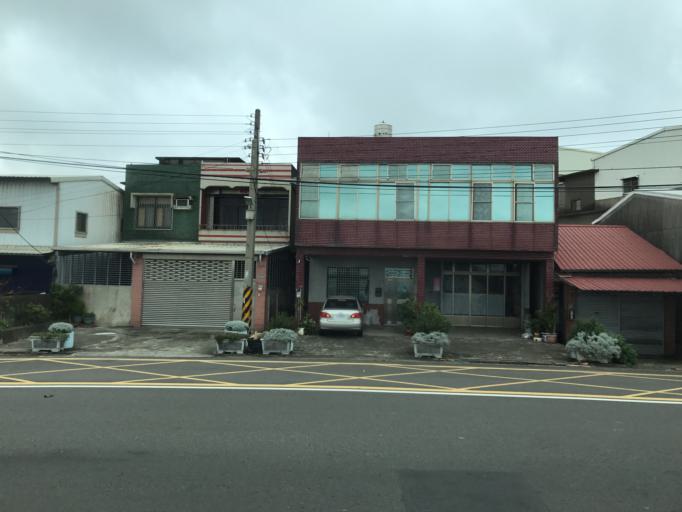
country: TW
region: Taiwan
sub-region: Hsinchu
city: Hsinchu
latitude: 24.8306
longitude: 120.9555
